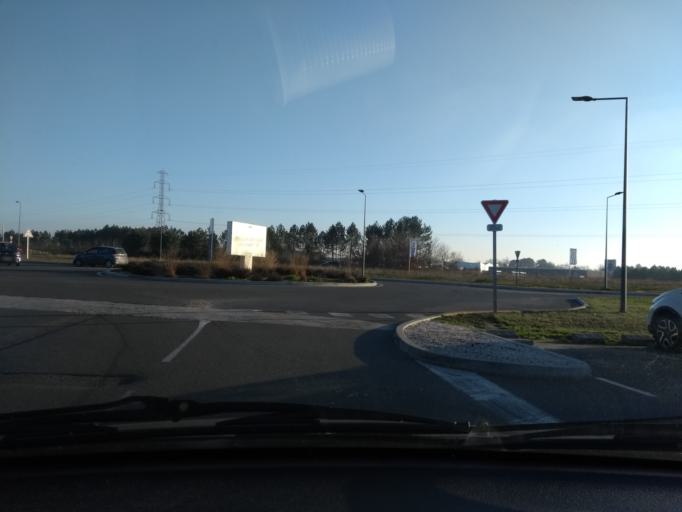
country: FR
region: Aquitaine
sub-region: Departement de la Gironde
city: Mios
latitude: 44.6181
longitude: -0.9183
